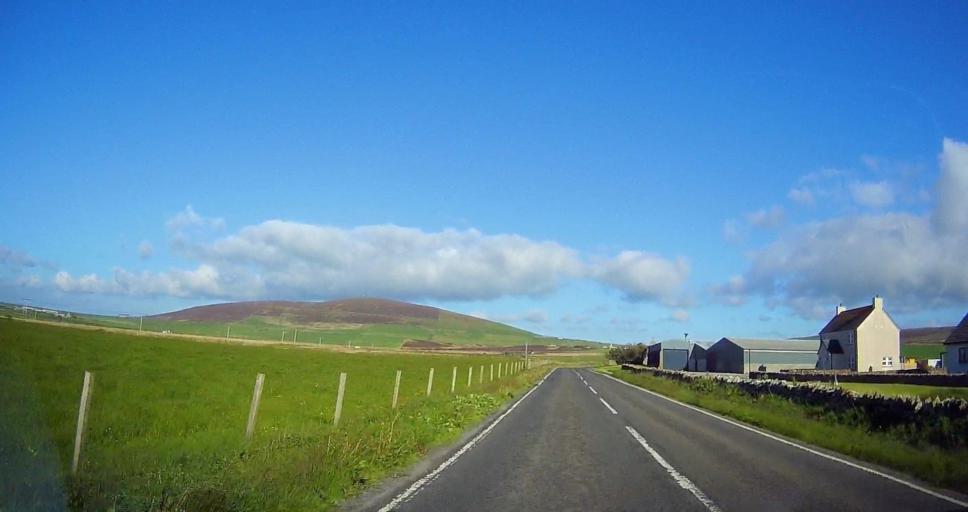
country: GB
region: Scotland
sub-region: Orkney Islands
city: Orkney
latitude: 58.9917
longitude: -3.0720
